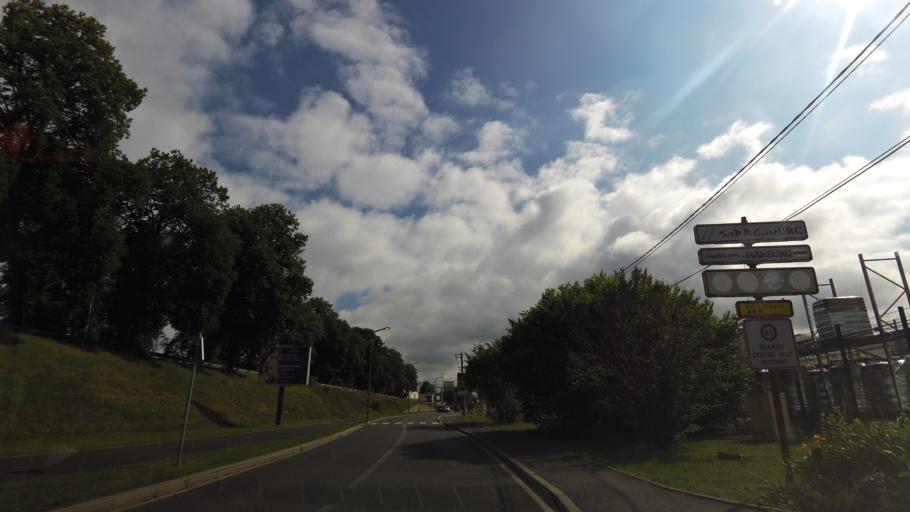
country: FR
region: Lorraine
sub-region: Departement de la Moselle
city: Sarrebourg
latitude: 48.7309
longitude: 7.0388
